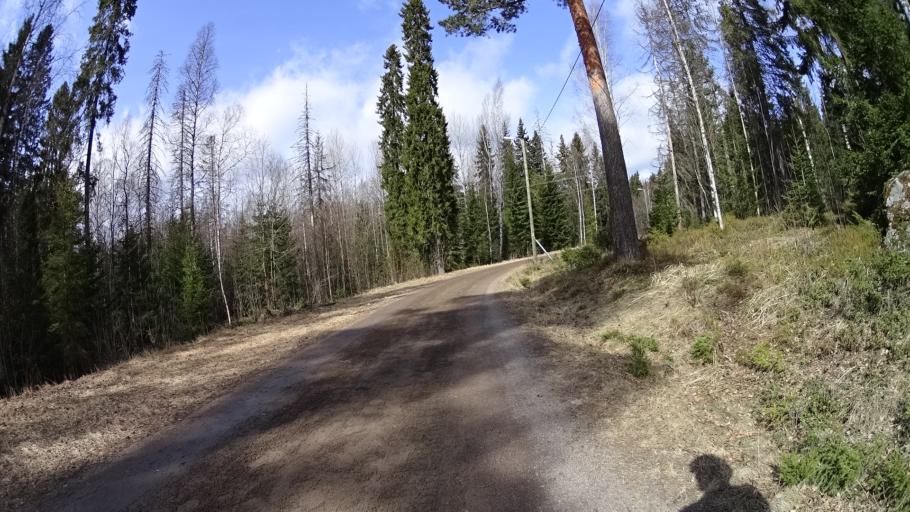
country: FI
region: Uusimaa
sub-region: Helsinki
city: Kilo
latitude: 60.2985
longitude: 24.8152
